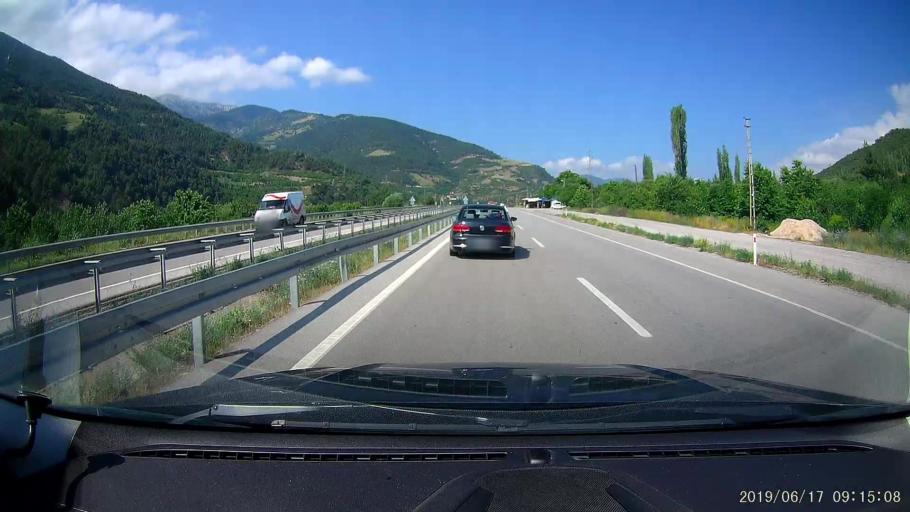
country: TR
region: Amasya
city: Akdag
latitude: 40.7489
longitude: 36.0441
